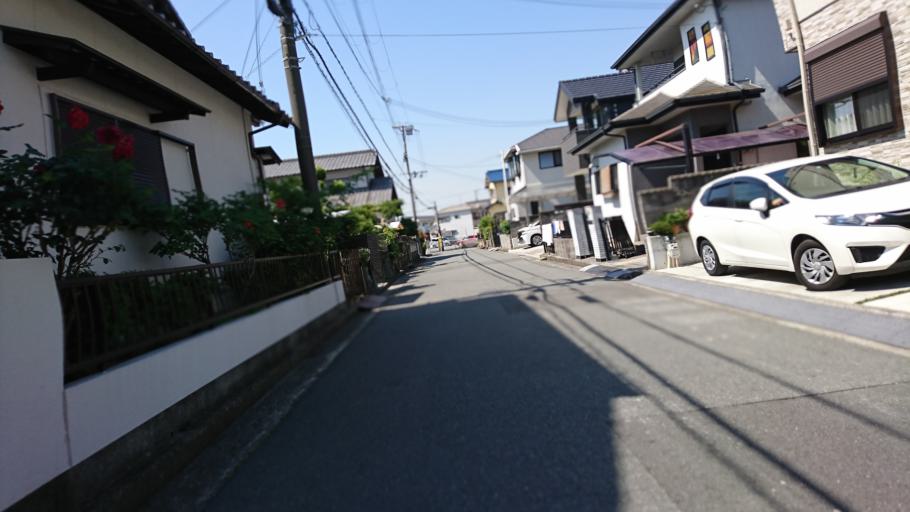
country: JP
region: Hyogo
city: Kakogawacho-honmachi
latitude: 34.7526
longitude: 134.8671
